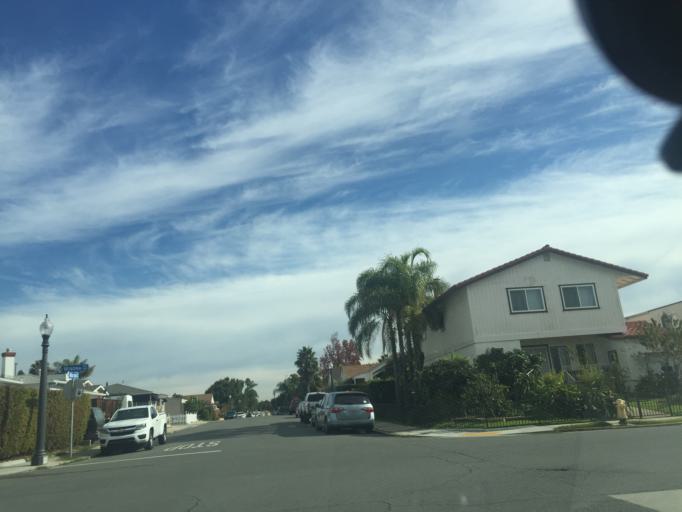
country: US
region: California
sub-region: San Diego County
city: Lemon Grove
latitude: 32.7610
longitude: -117.0868
